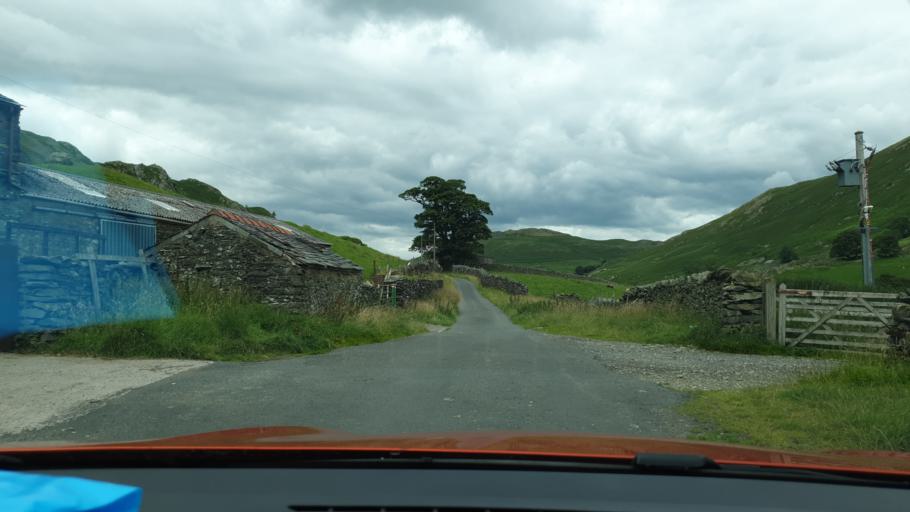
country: GB
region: England
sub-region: Cumbria
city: Ambleside
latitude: 54.5499
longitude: -2.8757
